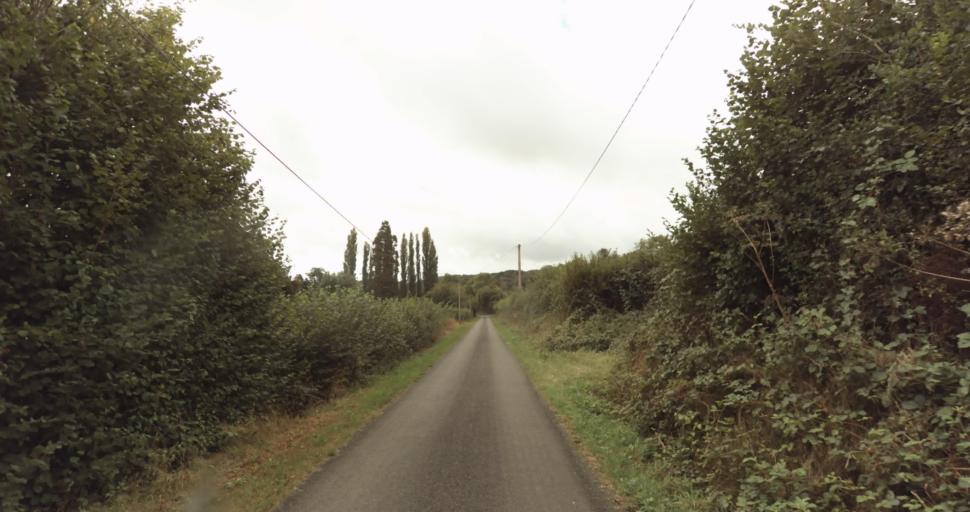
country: FR
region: Lower Normandy
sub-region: Departement de l'Orne
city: Gace
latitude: 48.8538
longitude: 0.2838
